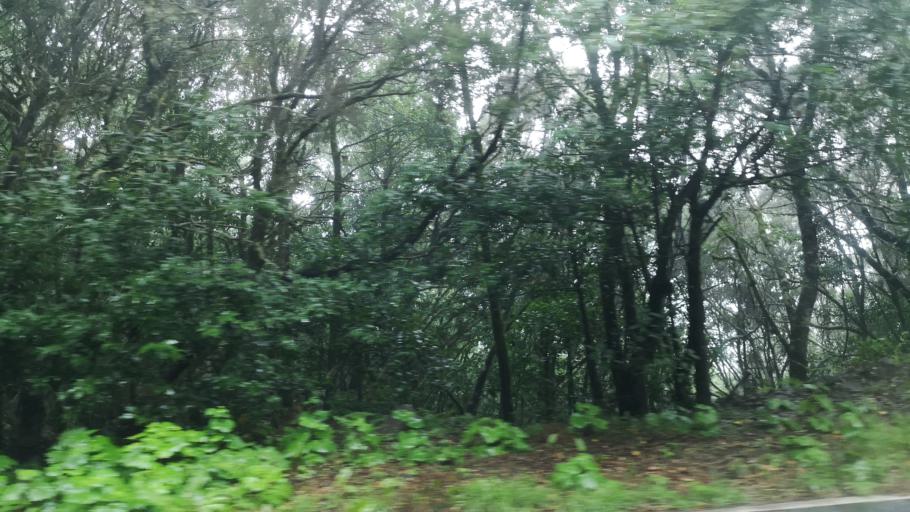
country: ES
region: Canary Islands
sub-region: Provincia de Santa Cruz de Tenerife
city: Hermigua
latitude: 28.1193
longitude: -17.2183
